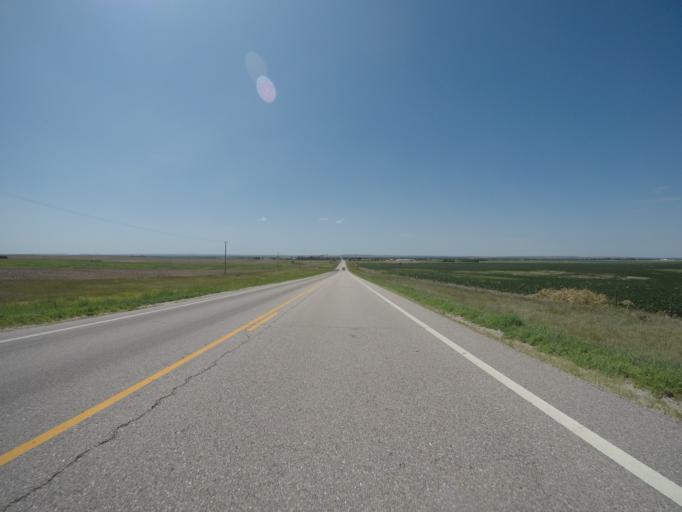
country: US
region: Kansas
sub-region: Osborne County
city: Osborne
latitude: 39.4646
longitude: -98.6945
